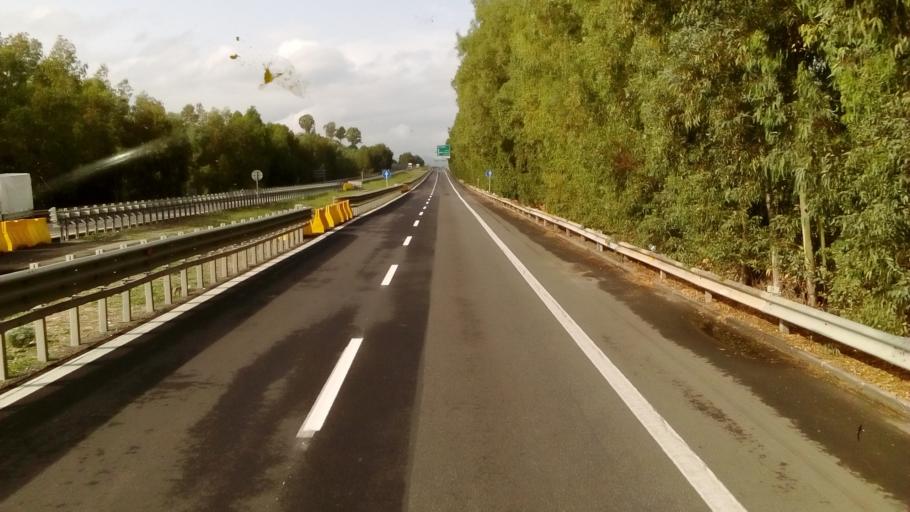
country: IT
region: Sicily
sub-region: Catania
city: Raddusa
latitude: 37.5429
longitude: 14.5469
